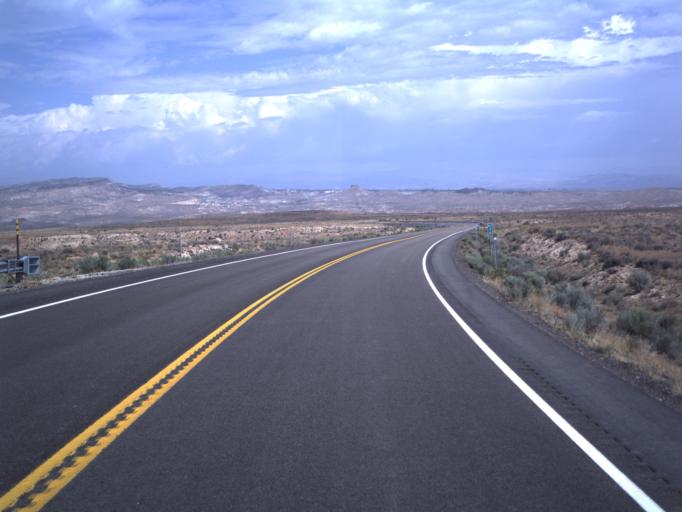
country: US
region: Utah
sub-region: Uintah County
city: Naples
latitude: 40.2766
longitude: -109.4659
